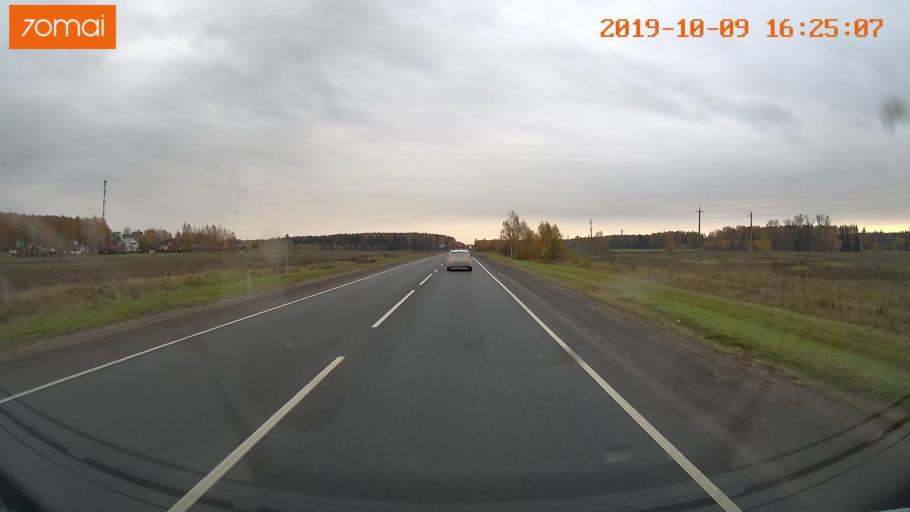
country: RU
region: Kostroma
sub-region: Kostromskoy Rayon
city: Kostroma
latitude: 57.6454
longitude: 40.9169
